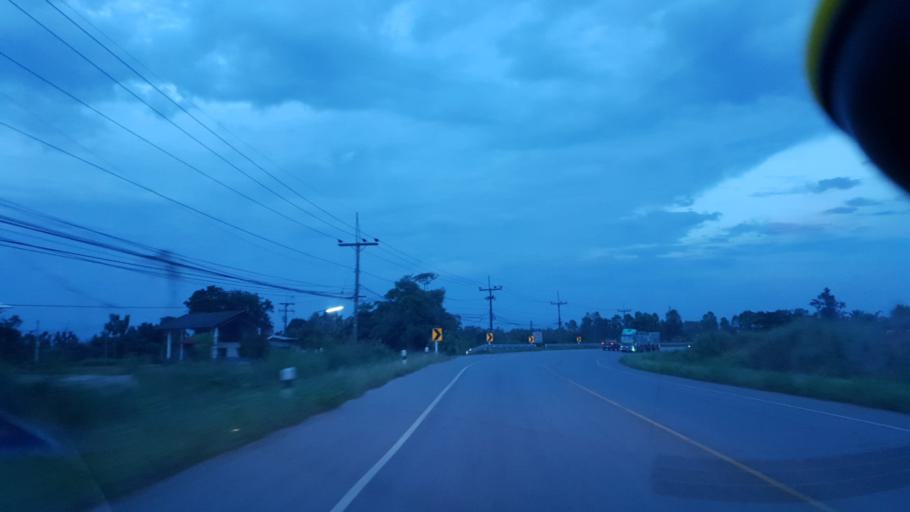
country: TH
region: Chiang Rai
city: Wiang Chiang Rung
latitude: 19.9697
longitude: 100.0127
